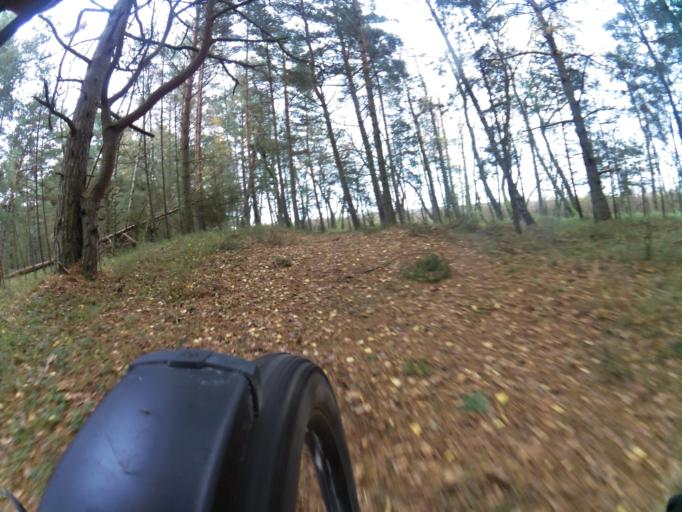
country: PL
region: Pomeranian Voivodeship
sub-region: Powiat leborski
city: Leba
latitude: 54.7731
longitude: 17.6472
